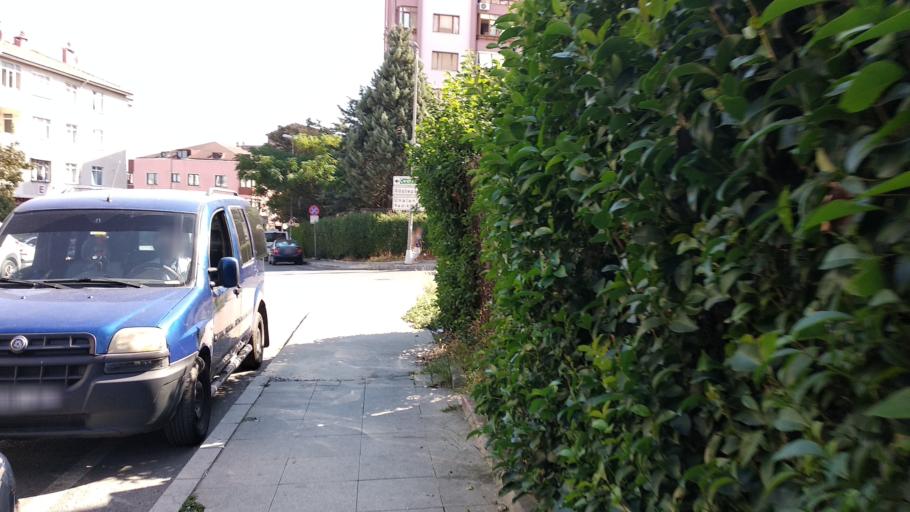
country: TR
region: Istanbul
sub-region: Atasehir
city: Atasehir
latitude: 41.0014
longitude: 29.0768
